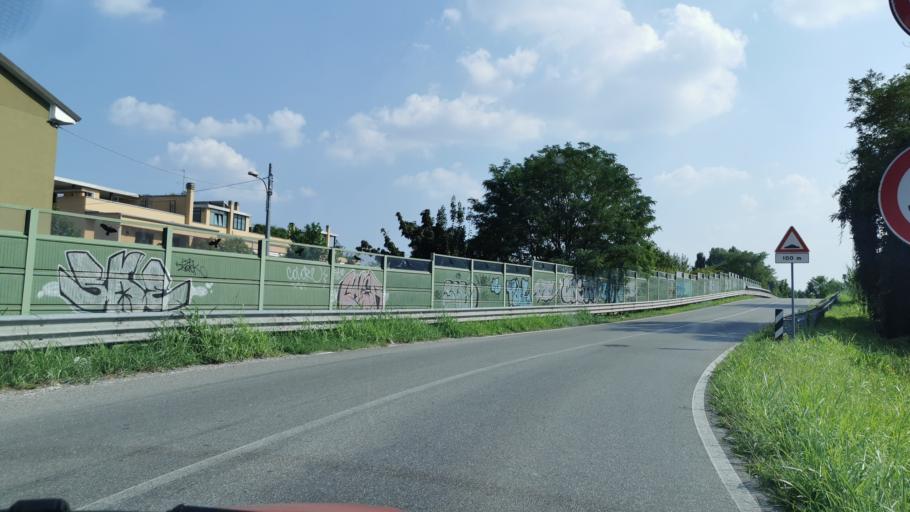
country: IT
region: Lombardy
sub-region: Provincia di Monza e Brianza
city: Muggio
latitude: 45.5877
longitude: 9.2201
